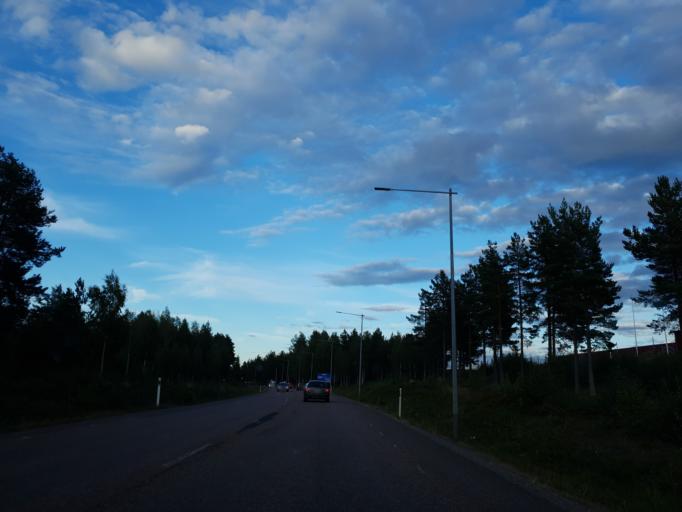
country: SE
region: Gaevleborg
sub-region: Soderhamns Kommun
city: Soderhamn
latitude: 61.2912
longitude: 17.0642
